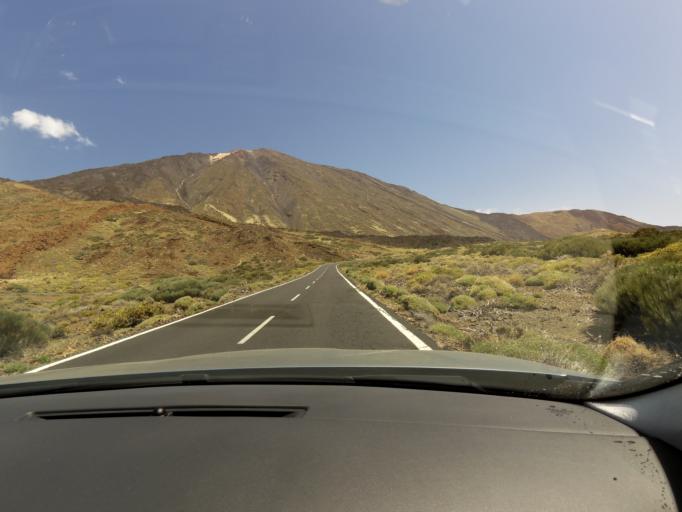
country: ES
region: Canary Islands
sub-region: Provincia de Santa Cruz de Tenerife
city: Vilaflor
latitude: 28.2416
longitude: -16.6302
